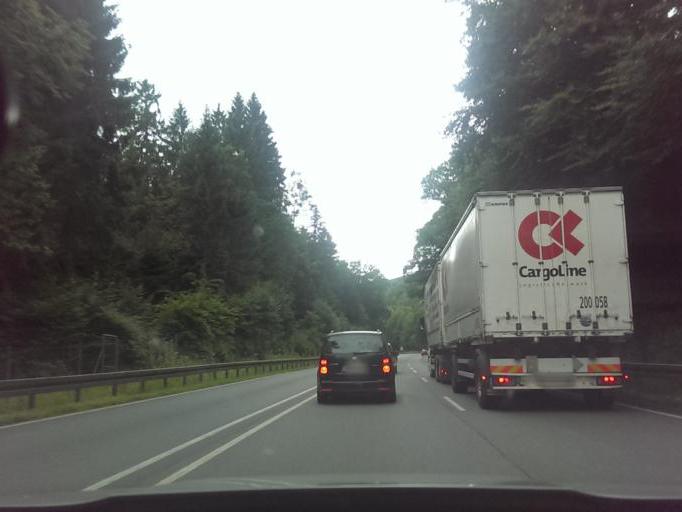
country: DE
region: North Rhine-Westphalia
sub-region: Regierungsbezirk Detmold
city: Horn
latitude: 51.8578
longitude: 8.9251
